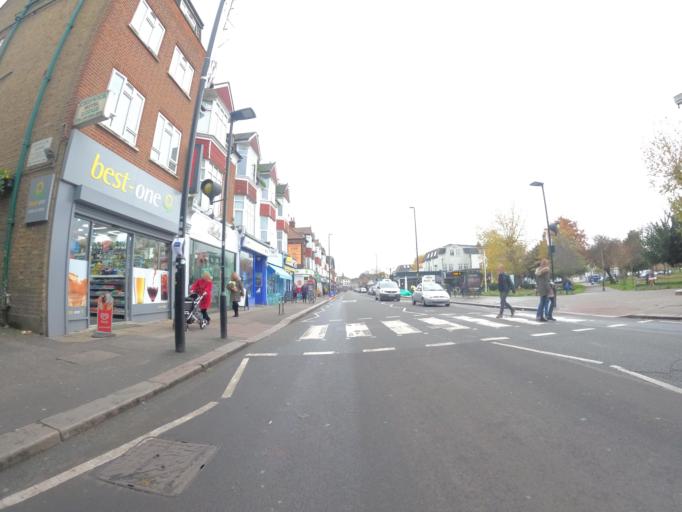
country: GB
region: England
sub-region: Greater London
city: Acton
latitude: 51.4950
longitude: -0.2552
